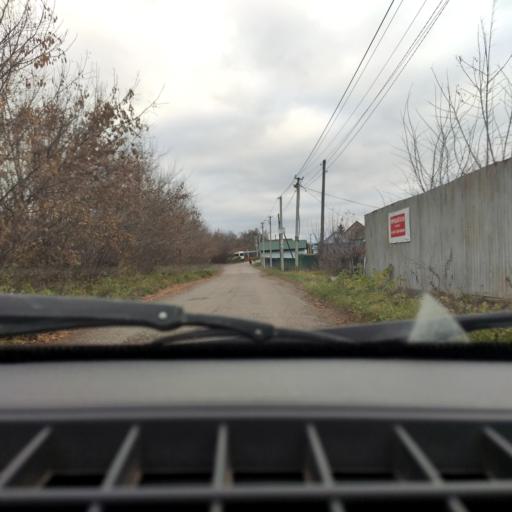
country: RU
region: Bashkortostan
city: Avdon
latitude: 54.6395
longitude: 55.7314
